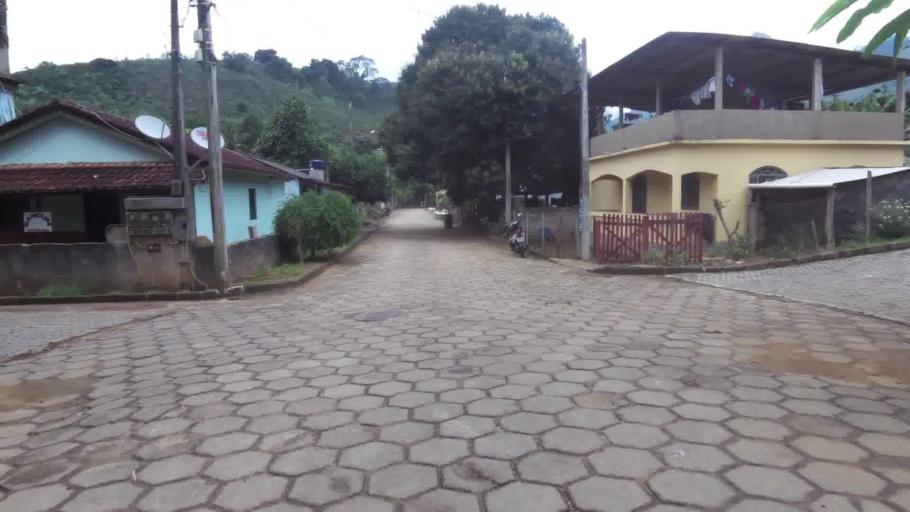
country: BR
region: Espirito Santo
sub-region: Iconha
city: Iconha
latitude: -20.7651
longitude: -40.8350
